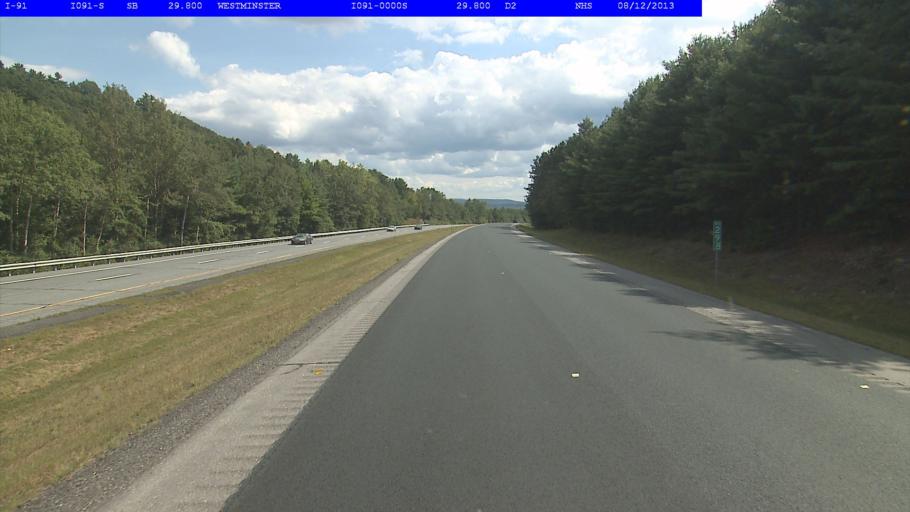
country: US
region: Vermont
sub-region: Windham County
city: Bellows Falls
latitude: 43.1080
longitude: -72.4558
